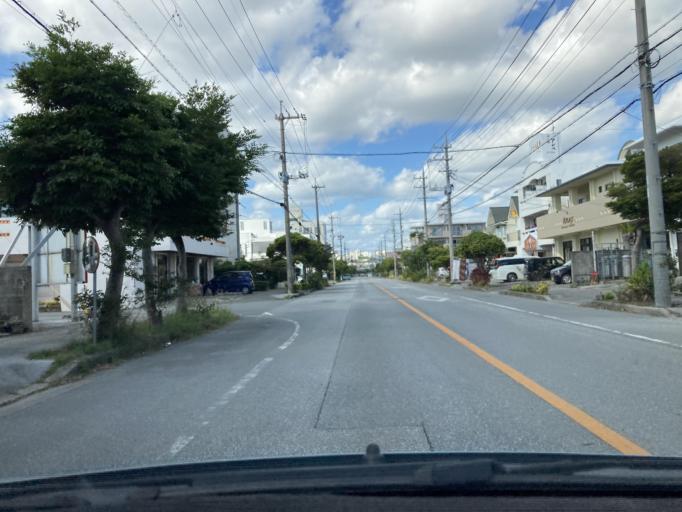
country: JP
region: Okinawa
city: Okinawa
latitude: 26.3200
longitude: 127.8358
